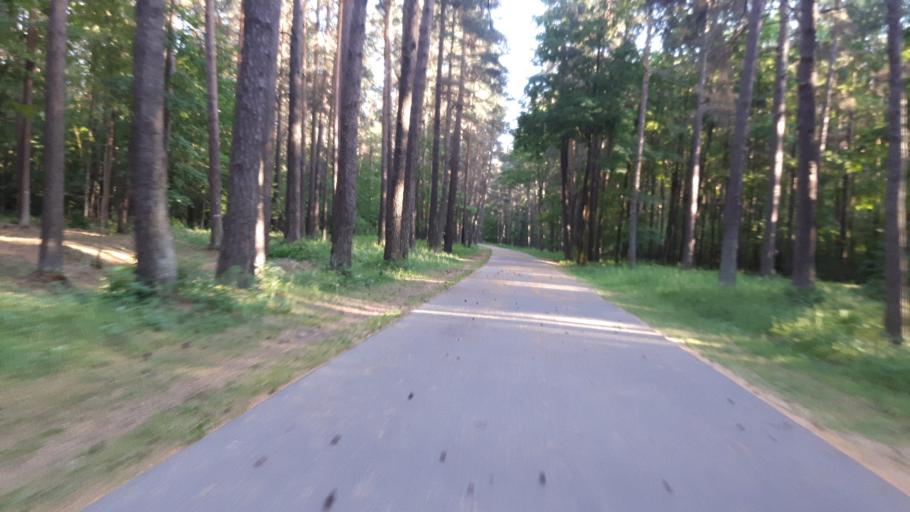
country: LV
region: Riga
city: Jaunciems
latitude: 57.0050
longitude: 24.1452
